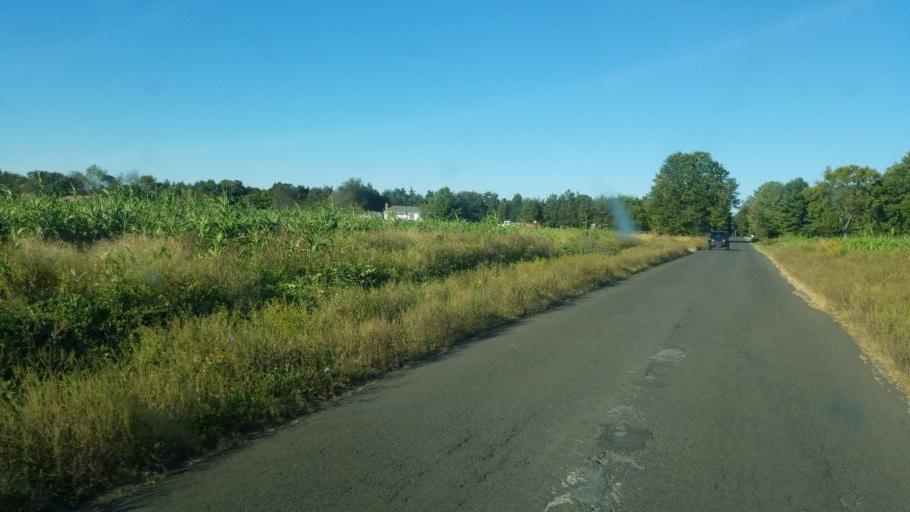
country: US
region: Virginia
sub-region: Fauquier County
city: Bealeton
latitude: 38.6012
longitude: -77.7578
